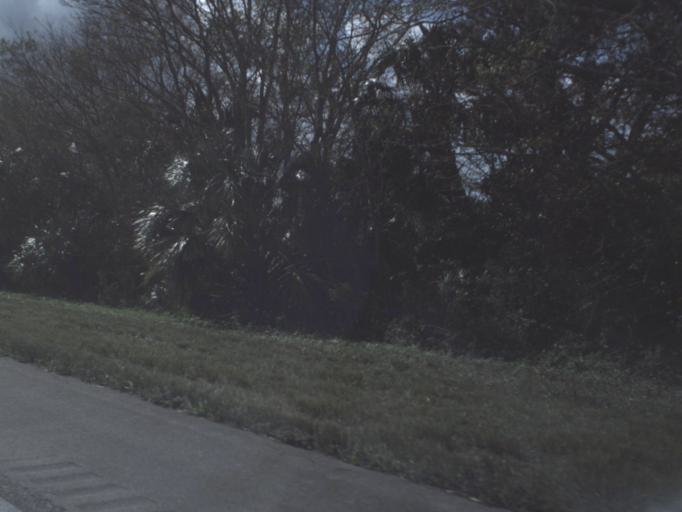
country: US
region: Florida
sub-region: Brevard County
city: Port Saint John
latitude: 28.4391
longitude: -80.8625
